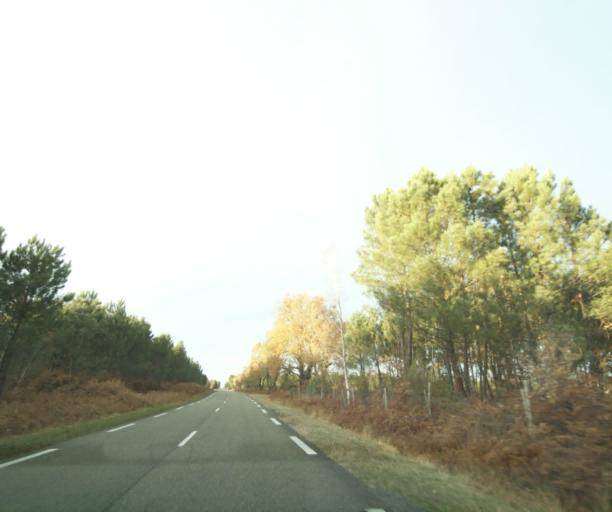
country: FR
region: Aquitaine
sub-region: Departement des Landes
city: Gabarret
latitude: 44.1209
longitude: -0.1072
